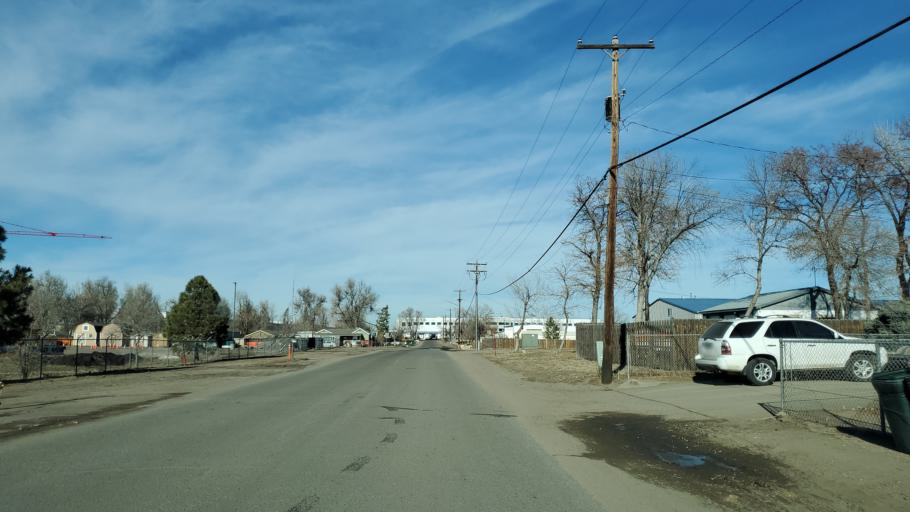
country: US
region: Colorado
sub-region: Adams County
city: Derby
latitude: 39.8531
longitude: -104.8937
